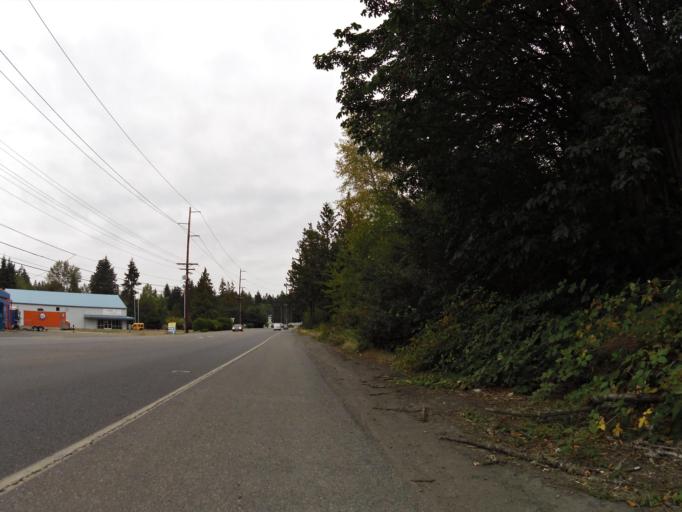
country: US
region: Washington
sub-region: Jefferson County
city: Port Hadlock-Irondale
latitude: 48.0414
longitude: -122.7891
